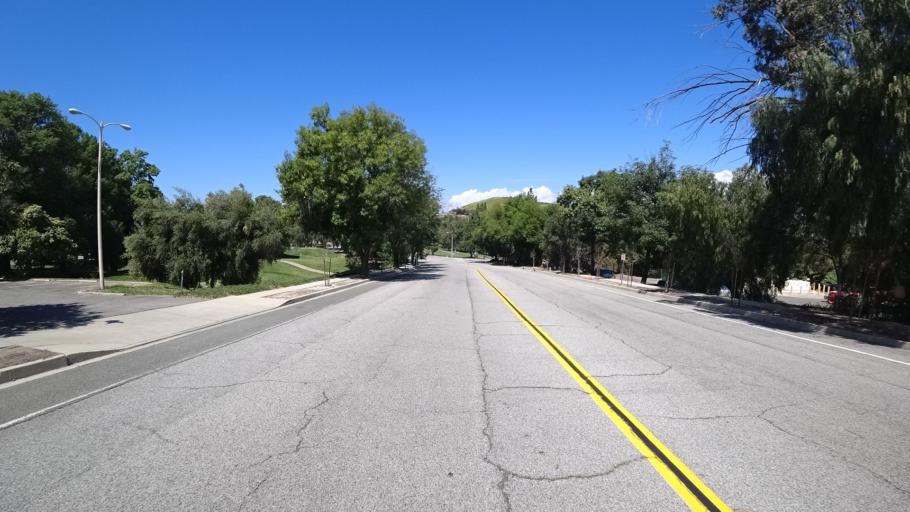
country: US
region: California
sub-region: Ventura County
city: Moorpark
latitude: 34.2359
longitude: -118.8432
